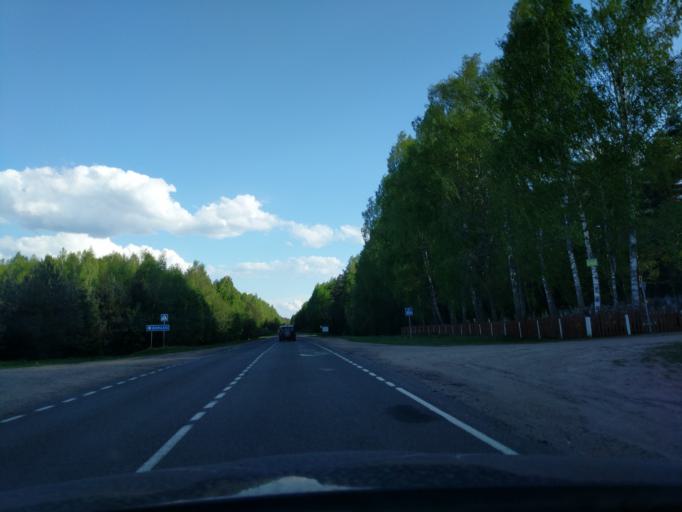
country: BY
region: Minsk
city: Kryvichy
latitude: 54.6056
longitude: 27.1824
